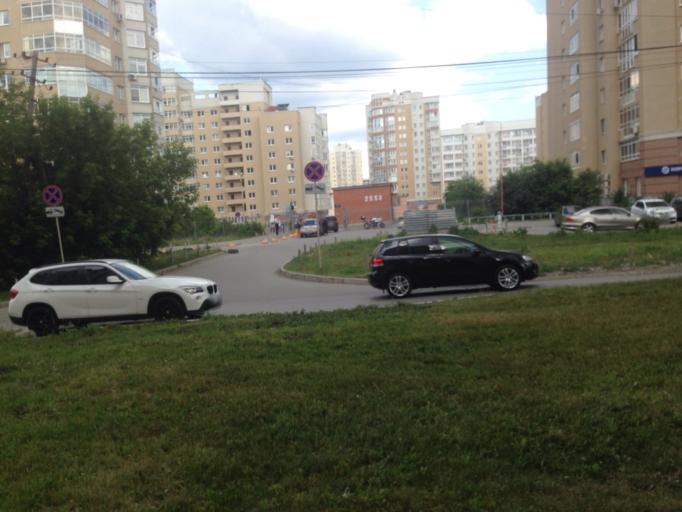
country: RU
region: Sverdlovsk
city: Yekaterinburg
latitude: 56.8057
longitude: 60.5991
